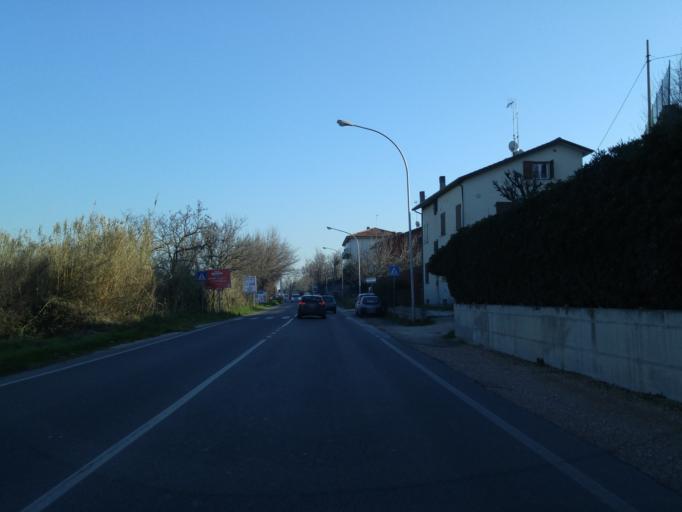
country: IT
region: The Marches
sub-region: Provincia di Pesaro e Urbino
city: Fano
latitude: 43.8556
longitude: 13.0006
